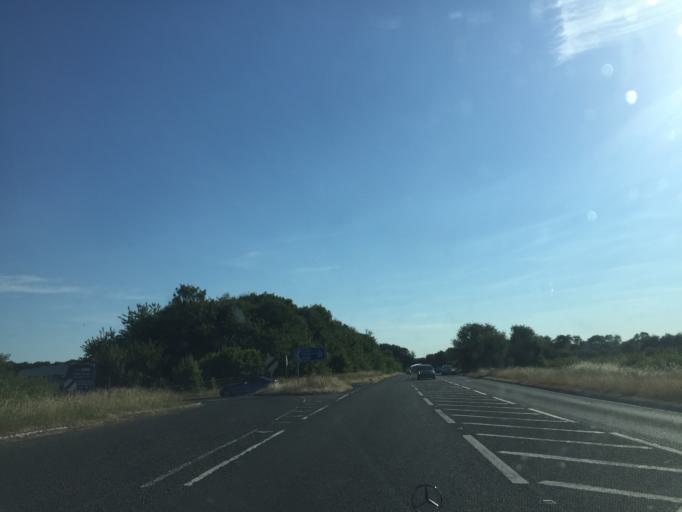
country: GB
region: England
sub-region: Oxfordshire
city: Chinnor
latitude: 51.6743
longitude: -0.9556
